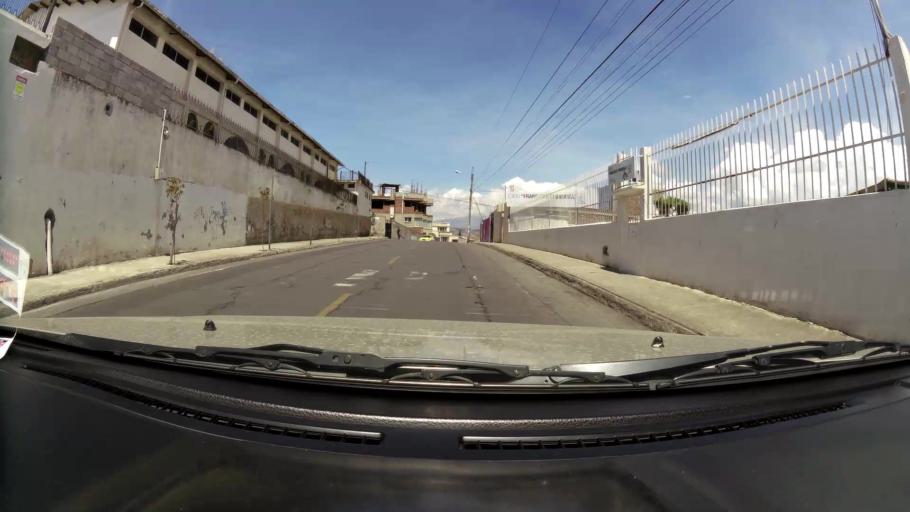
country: EC
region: Chimborazo
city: Riobamba
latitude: -1.6622
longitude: -78.6567
